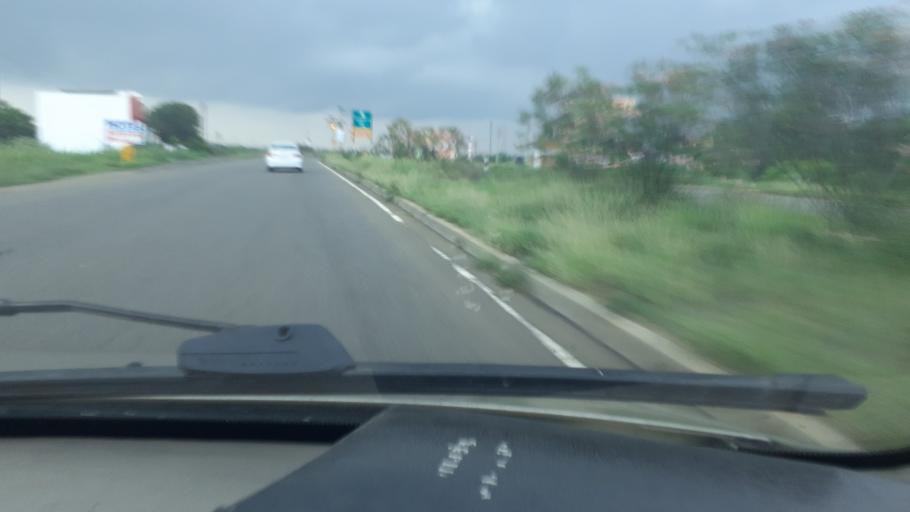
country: IN
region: Tamil Nadu
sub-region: Thoothukkudi
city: Kovilpatti
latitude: 9.1141
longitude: 77.8128
